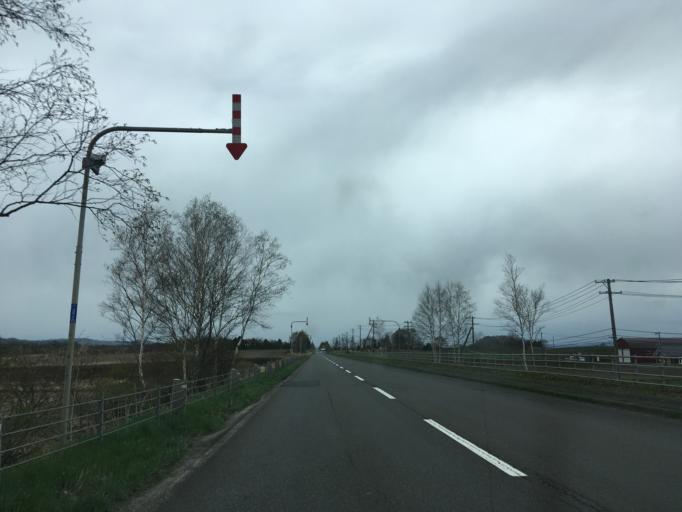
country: JP
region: Hokkaido
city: Chitose
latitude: 42.9081
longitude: 141.8119
